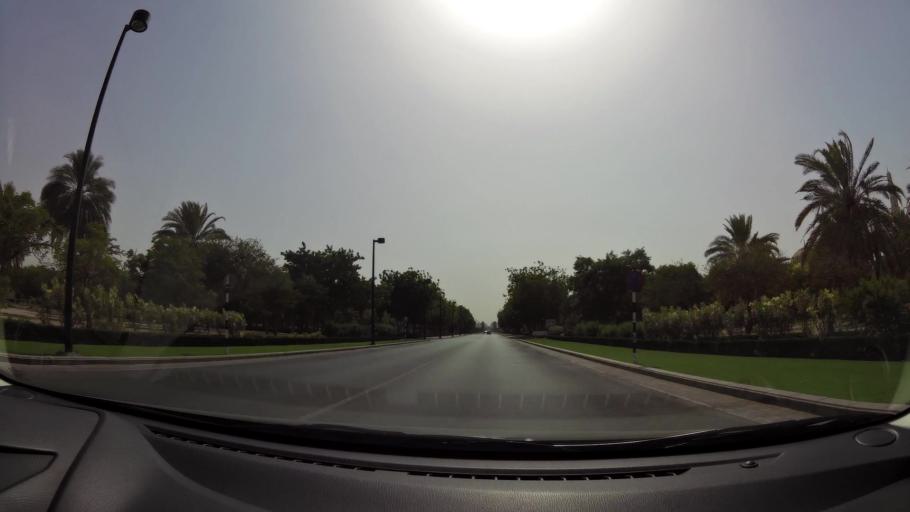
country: OM
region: Muhafazat Masqat
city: Bawshar
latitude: 23.5819
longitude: 58.3906
